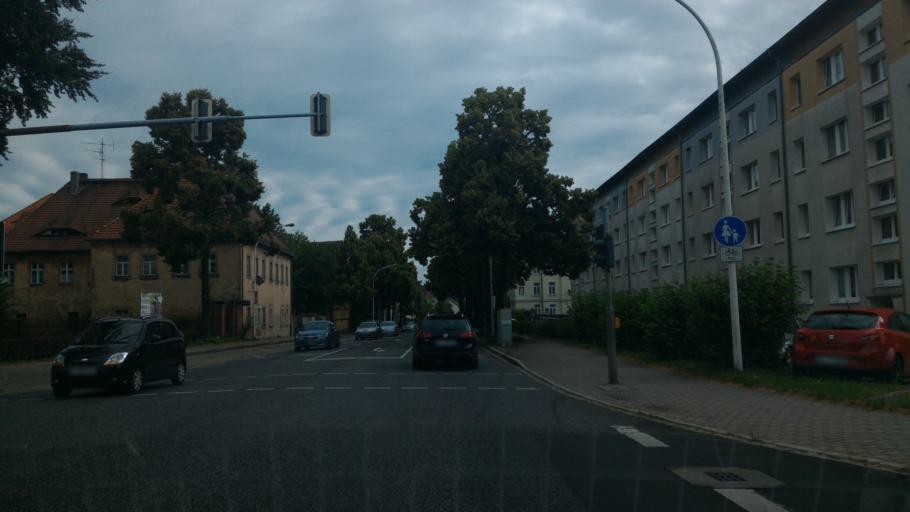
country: DE
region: Saxony
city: Zittau
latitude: 50.9004
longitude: 14.8211
